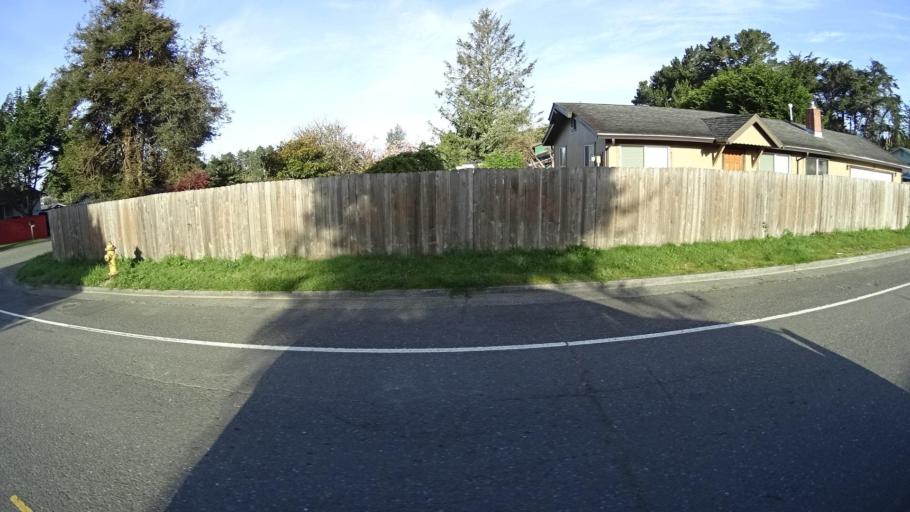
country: US
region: California
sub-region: Humboldt County
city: Humboldt Hill
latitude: 40.7178
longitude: -124.2032
